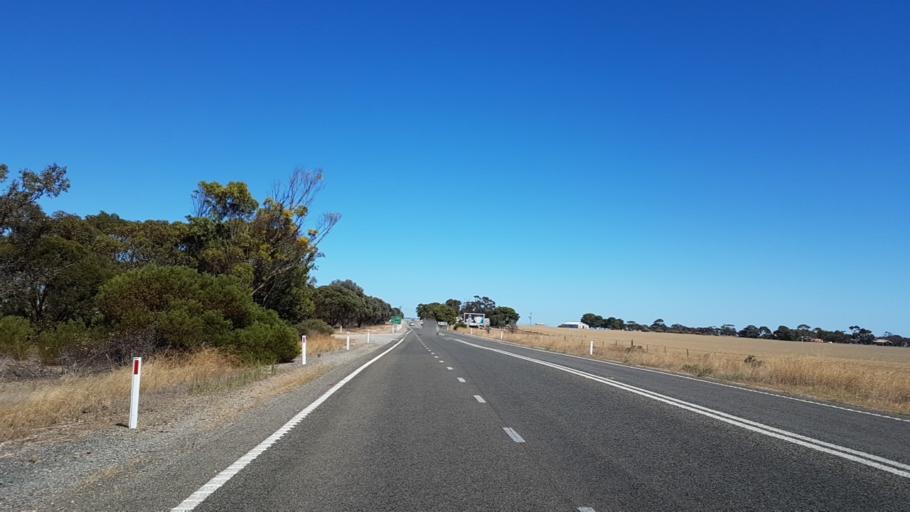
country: AU
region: South Australia
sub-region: Copper Coast
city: Kadina
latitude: -34.0605
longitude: 138.0420
